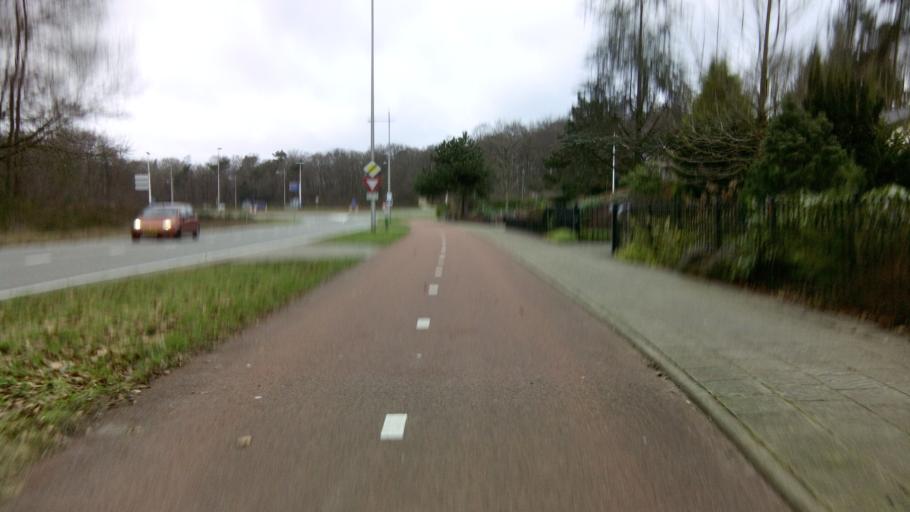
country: NL
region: Utrecht
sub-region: Gemeente Amersfoort
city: Amersfoort
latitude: 52.1398
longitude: 5.3599
